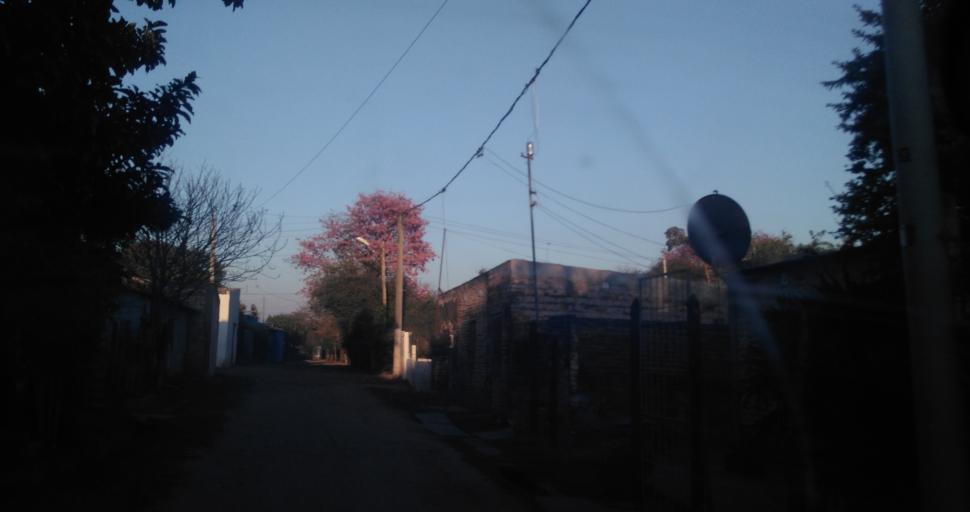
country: AR
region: Chaco
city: Fontana
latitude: -27.4274
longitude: -59.0161
